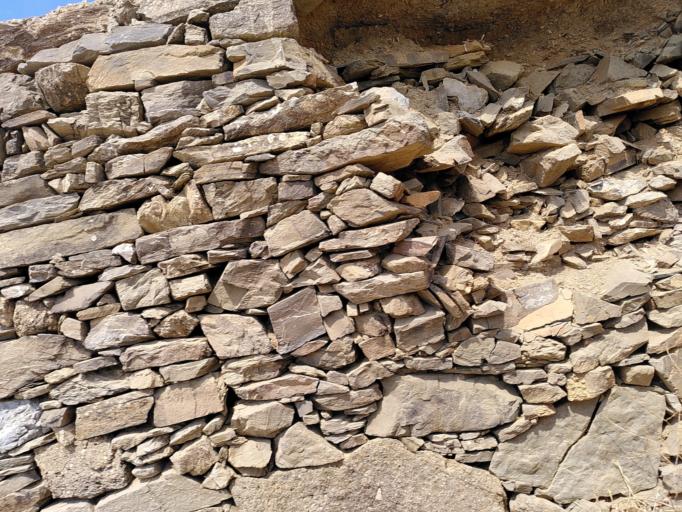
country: GR
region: South Aegean
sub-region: Nomos Kykladon
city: Amorgos
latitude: 36.9156
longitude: 25.9809
